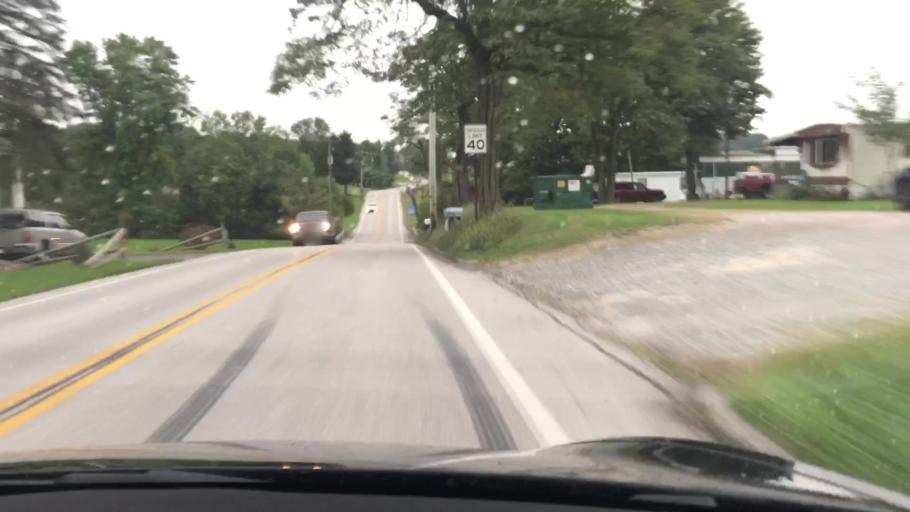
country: US
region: Pennsylvania
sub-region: York County
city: Dover
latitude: 39.9793
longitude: -76.8801
